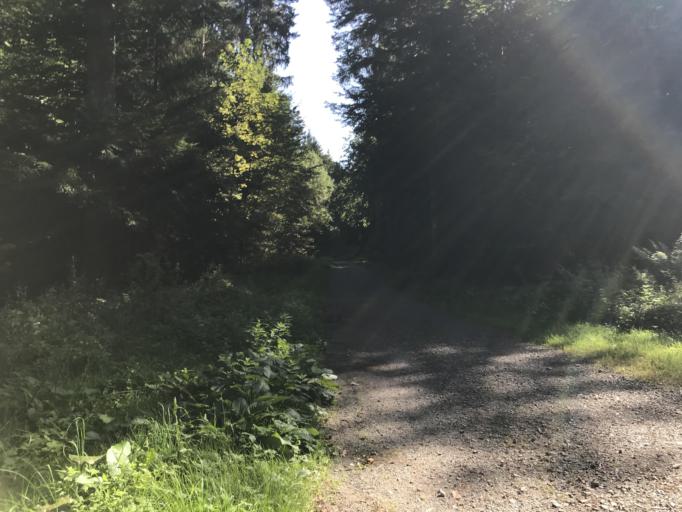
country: DE
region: Baden-Wuerttemberg
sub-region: Karlsruhe Region
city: Calw
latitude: 48.7035
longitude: 8.7244
